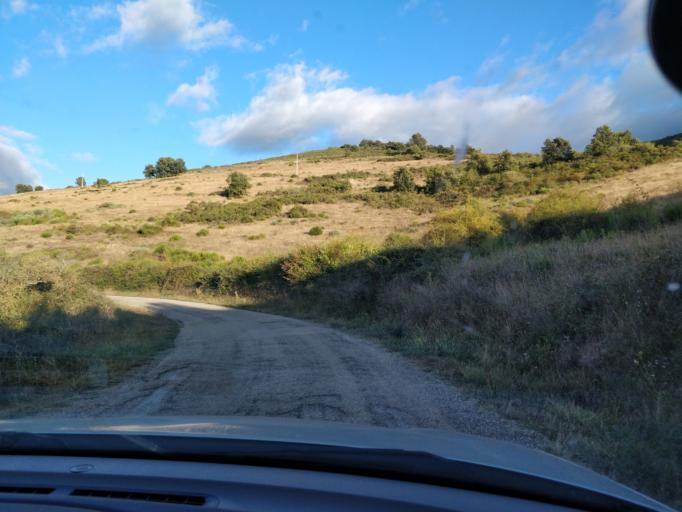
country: ES
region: Castille and Leon
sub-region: Provincia de Leon
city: Borrenes
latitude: 42.4852
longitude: -6.7007
